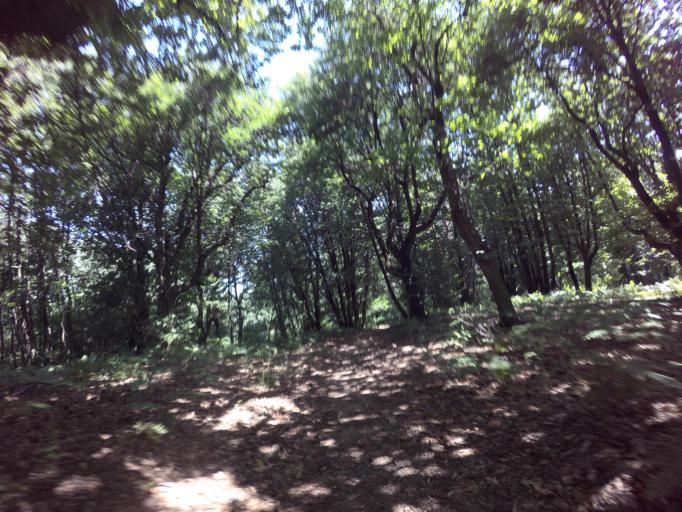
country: IT
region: Piedmont
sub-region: Provincia di Cuneo
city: Pianfei
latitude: 44.3410
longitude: 7.7074
